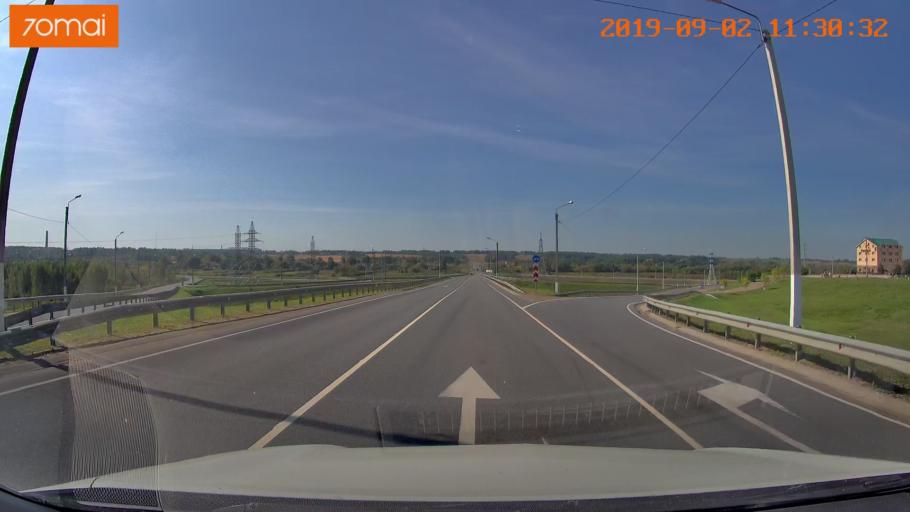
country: RU
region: Smolensk
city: Roslavl'
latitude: 53.9832
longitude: 32.8321
